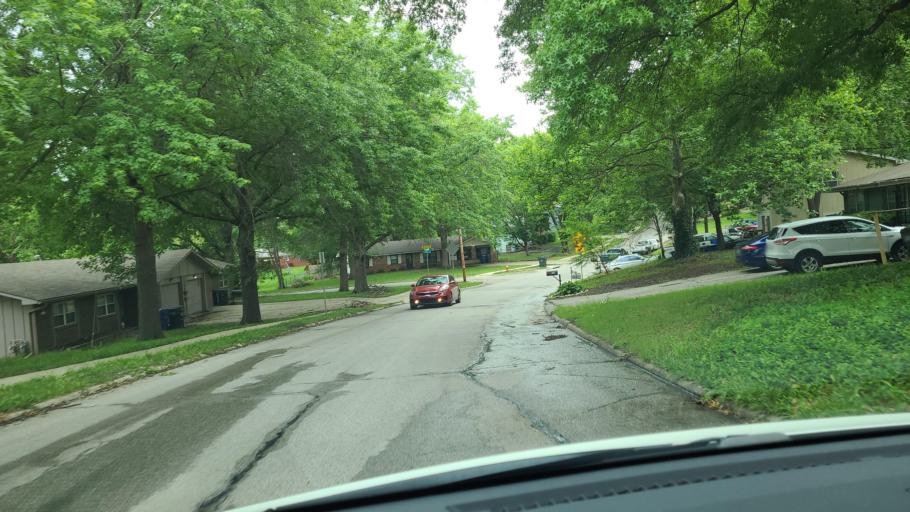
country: US
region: Kansas
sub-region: Douglas County
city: Lawrence
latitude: 38.9375
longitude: -95.2547
